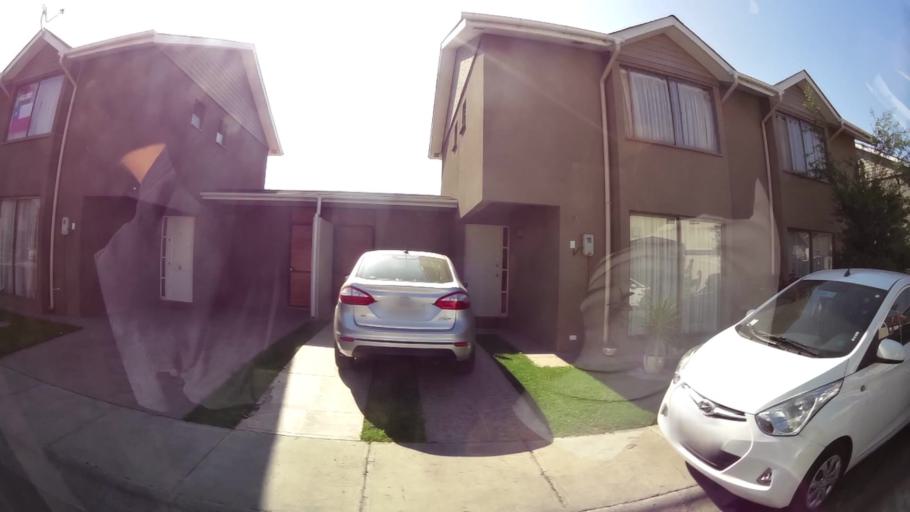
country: CL
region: Santiago Metropolitan
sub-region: Provincia de Santiago
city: Lo Prado
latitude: -33.4831
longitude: -70.7694
